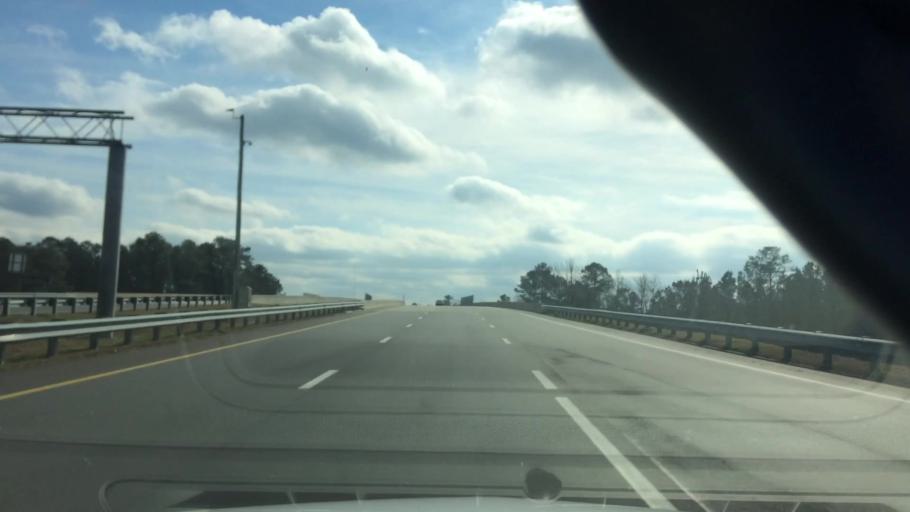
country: US
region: North Carolina
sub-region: Brunswick County
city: Leland
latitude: 34.2595
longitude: -78.0801
